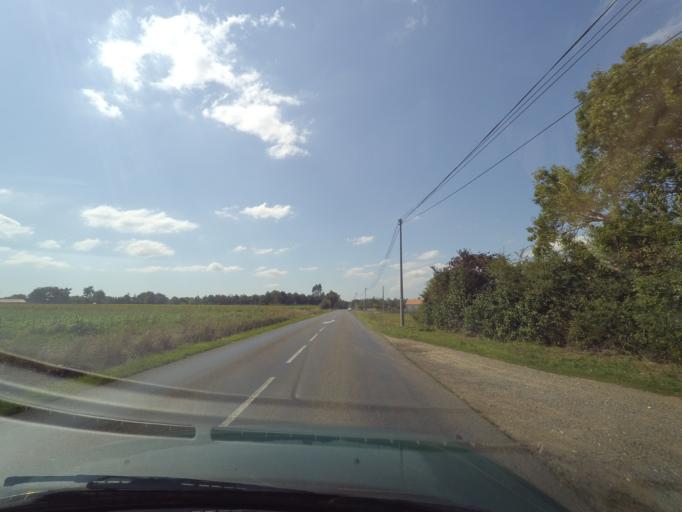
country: FR
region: Pays de la Loire
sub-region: Departement de la Loire-Atlantique
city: Saint-Lumine-de-Coutais
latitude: 47.0523
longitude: -1.7389
